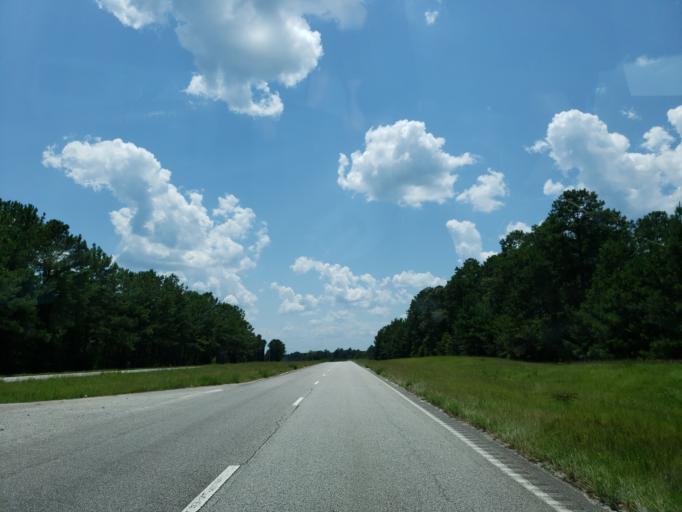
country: US
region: Mississippi
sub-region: Wayne County
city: Belmont
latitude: 31.3675
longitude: -88.4896
